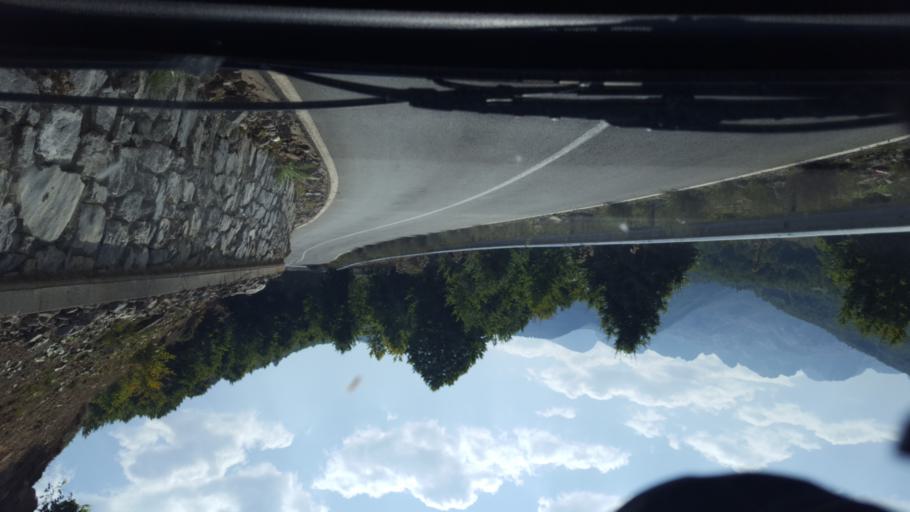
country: AL
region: Kukes
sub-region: Rrethi i Tropojes
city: Valbone
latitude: 42.5469
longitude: 19.7209
